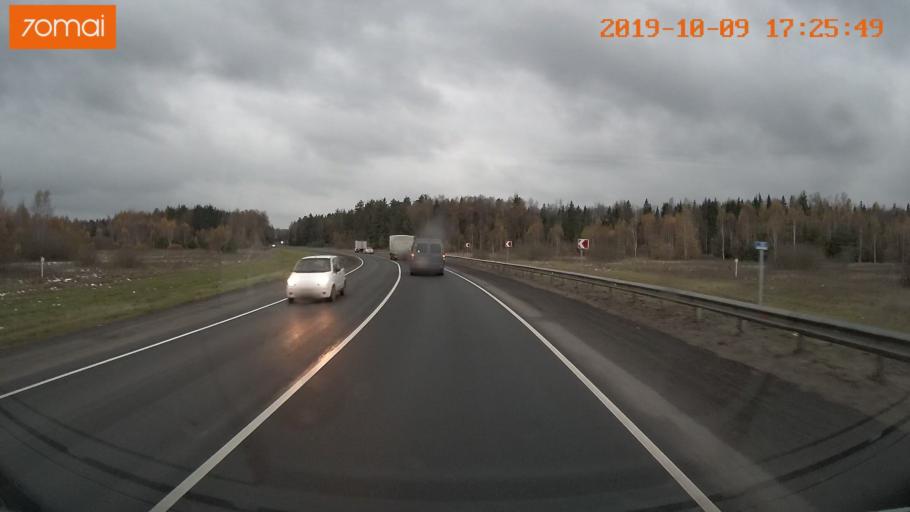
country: RU
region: Ivanovo
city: Furmanov
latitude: 57.1789
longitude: 41.0840
